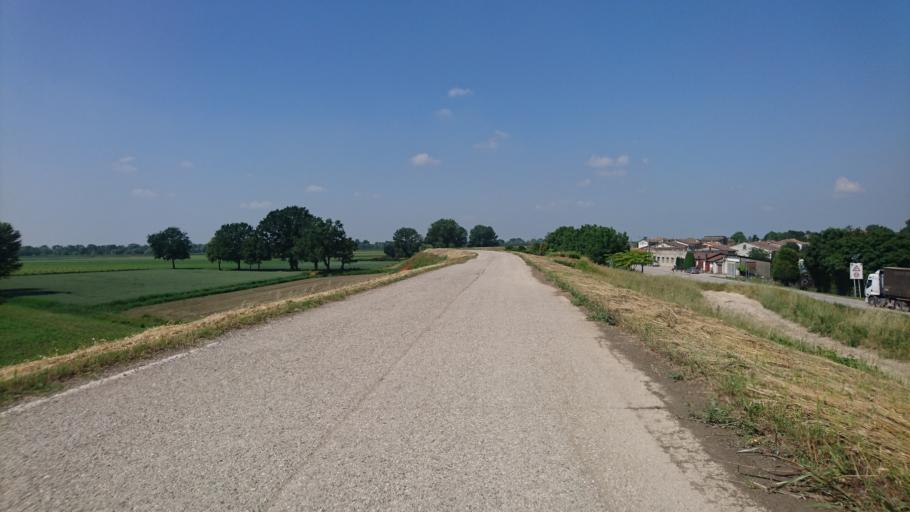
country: IT
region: Lombardy
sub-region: Provincia di Mantova
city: Sustinente
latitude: 45.0669
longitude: 11.0338
